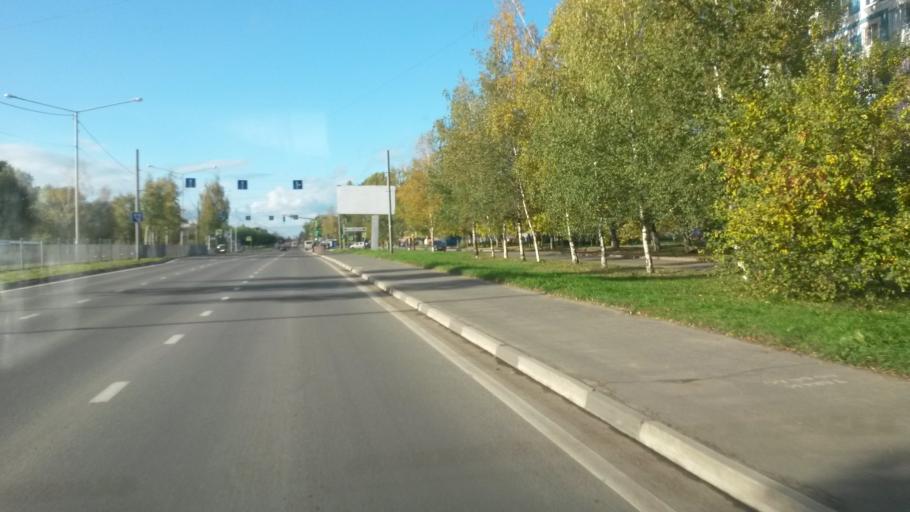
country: RU
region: Jaroslavl
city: Yaroslavl
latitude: 57.5669
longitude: 39.9286
